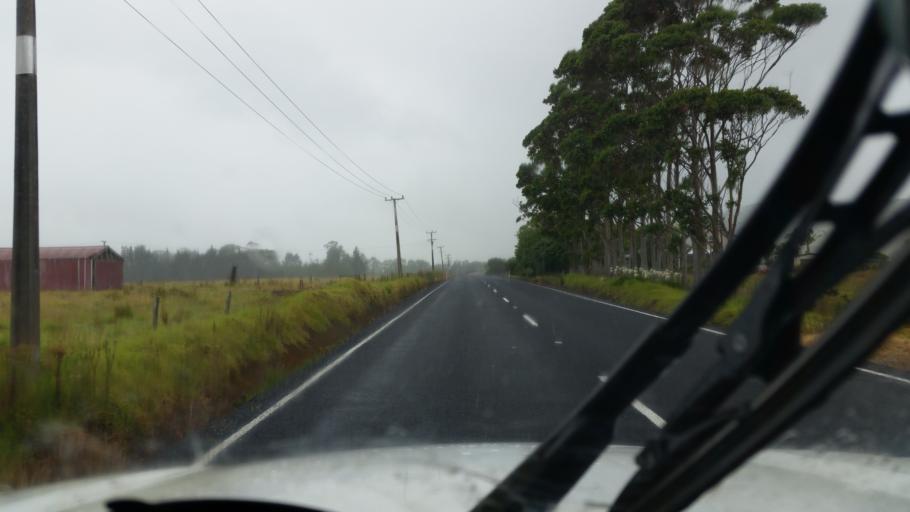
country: NZ
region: Northland
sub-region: Far North District
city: Ahipara
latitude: -35.1775
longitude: 173.1725
